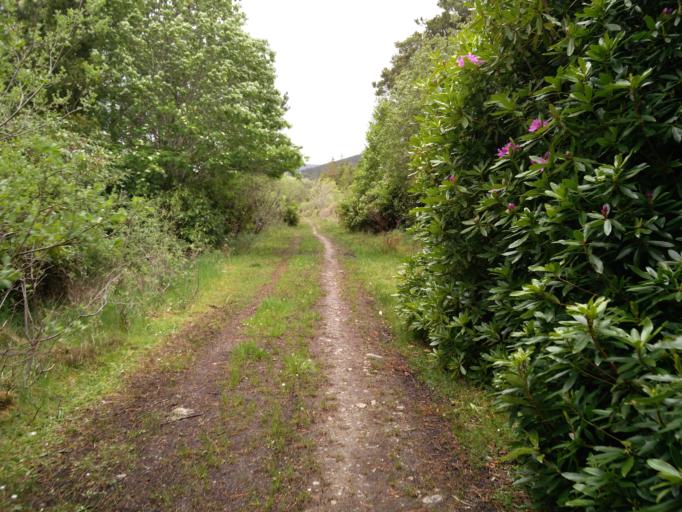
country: IE
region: Connaught
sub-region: Maigh Eo
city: Westport
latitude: 53.9859
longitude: -9.5707
